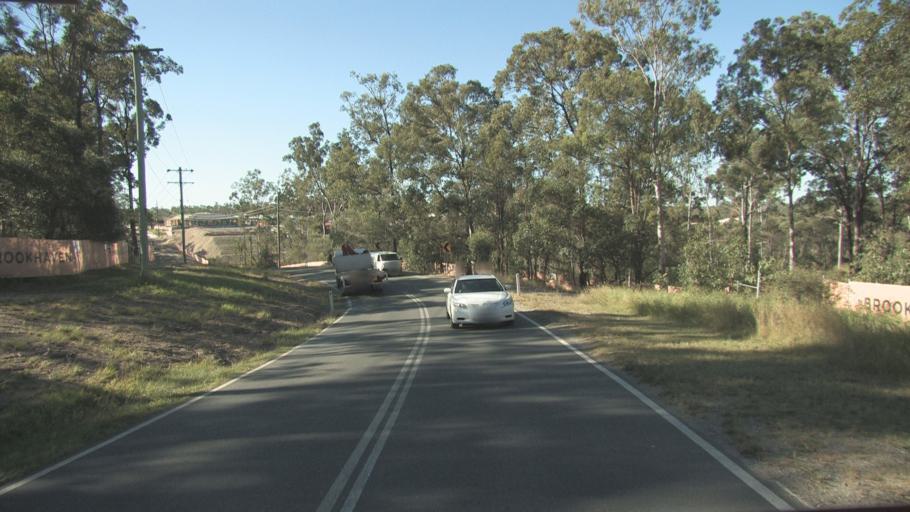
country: AU
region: Queensland
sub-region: Logan
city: Windaroo
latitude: -27.7340
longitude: 153.1624
